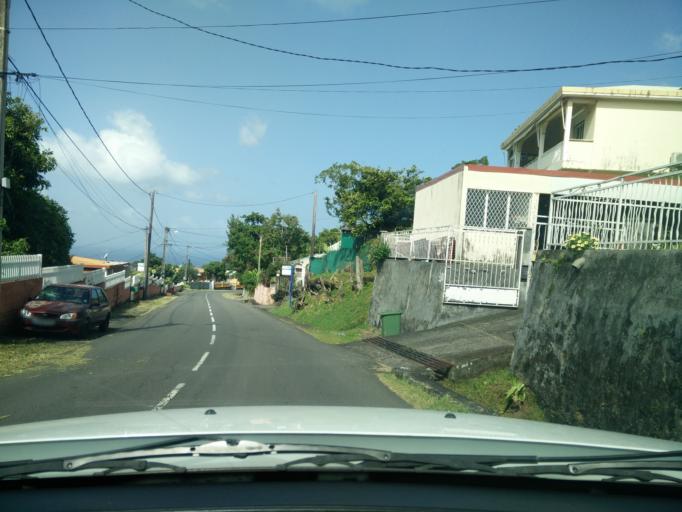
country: GP
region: Guadeloupe
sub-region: Guadeloupe
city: Gourbeyre
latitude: 16.0001
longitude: -61.6976
